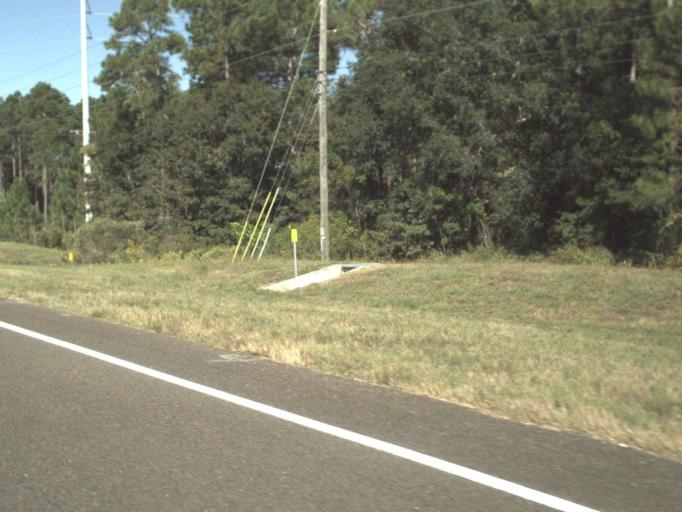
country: US
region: Florida
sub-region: Walton County
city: Seaside
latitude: 30.3573
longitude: -86.1280
